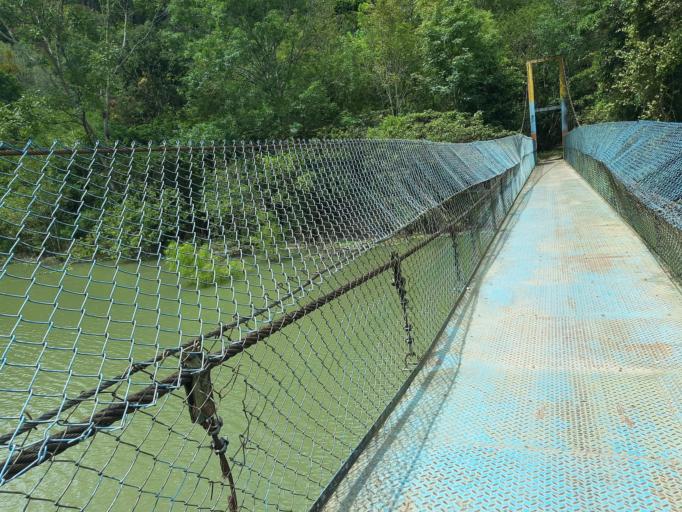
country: CO
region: Boyaca
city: Somondoco
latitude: 5.0070
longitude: -73.4006
